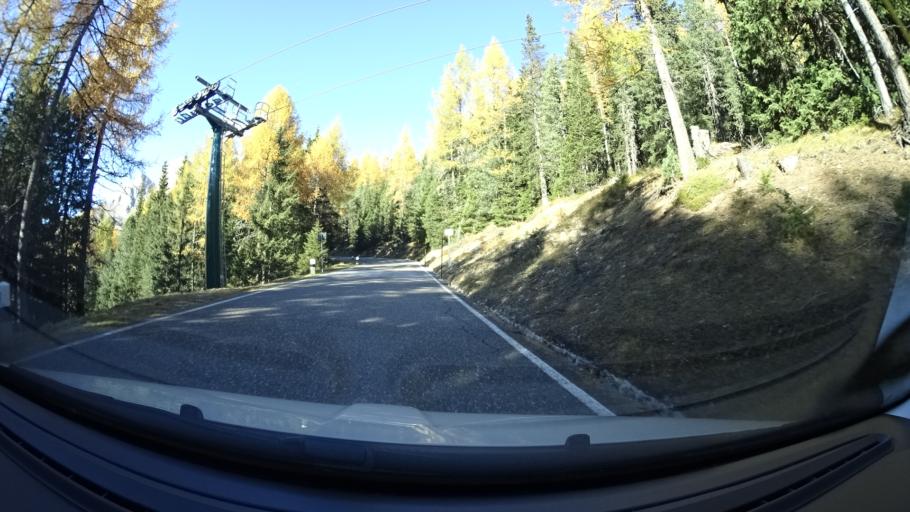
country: IT
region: Trentino-Alto Adige
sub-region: Provincia di Trento
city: Canazei
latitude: 46.4872
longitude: 11.7913
